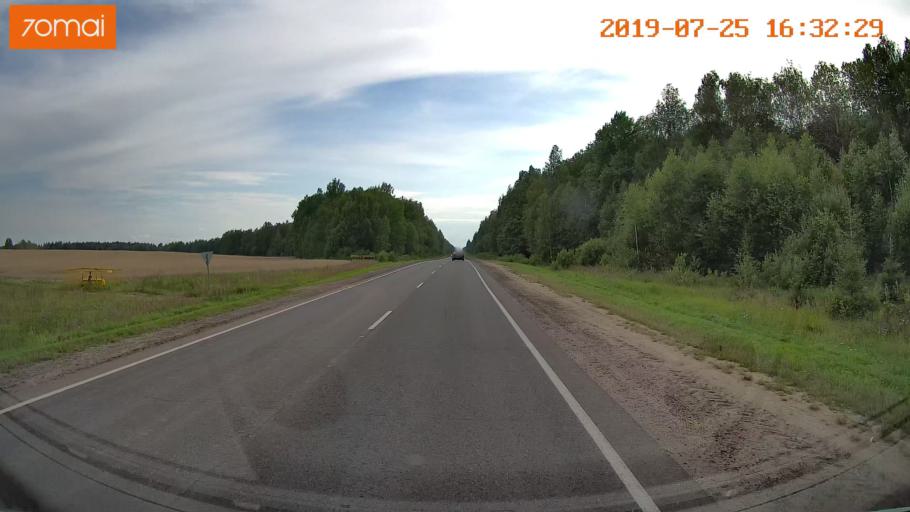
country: RU
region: Ivanovo
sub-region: Privolzhskiy Rayon
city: Ples
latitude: 57.4364
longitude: 41.4738
